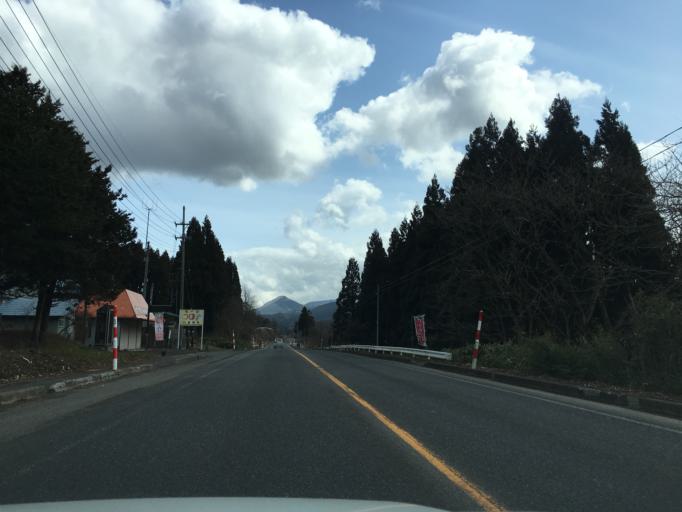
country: JP
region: Akita
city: Odate
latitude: 40.2239
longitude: 140.6037
